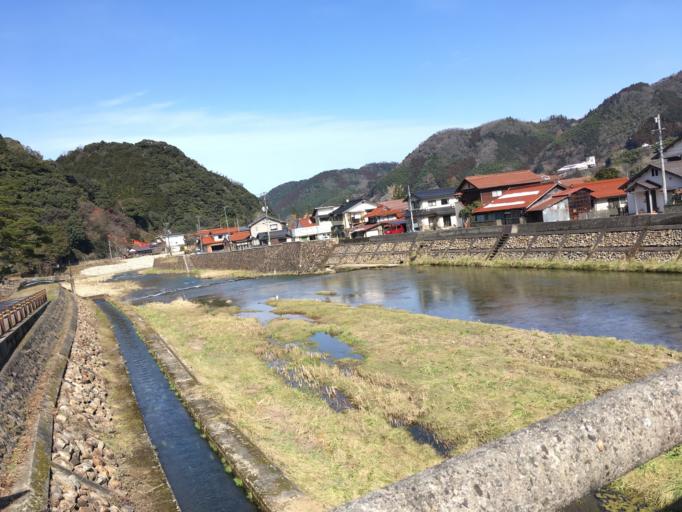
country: JP
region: Shimane
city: Masuda
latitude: 34.4624
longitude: 131.7699
